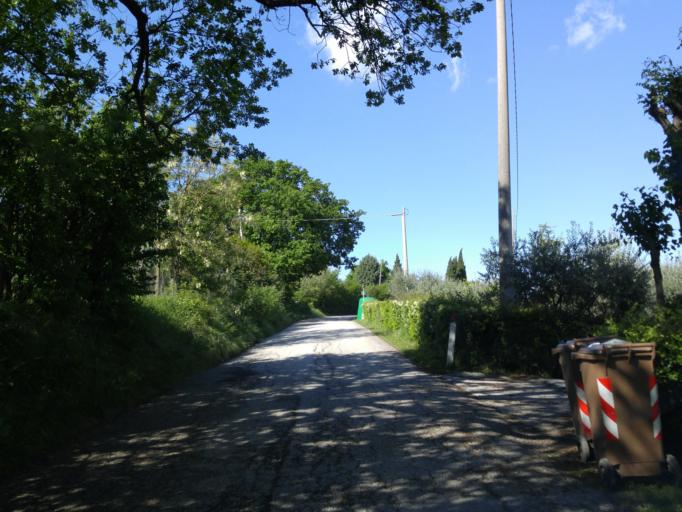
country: IT
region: The Marches
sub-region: Provincia di Pesaro e Urbino
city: Lucrezia
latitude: 43.7900
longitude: 12.9110
